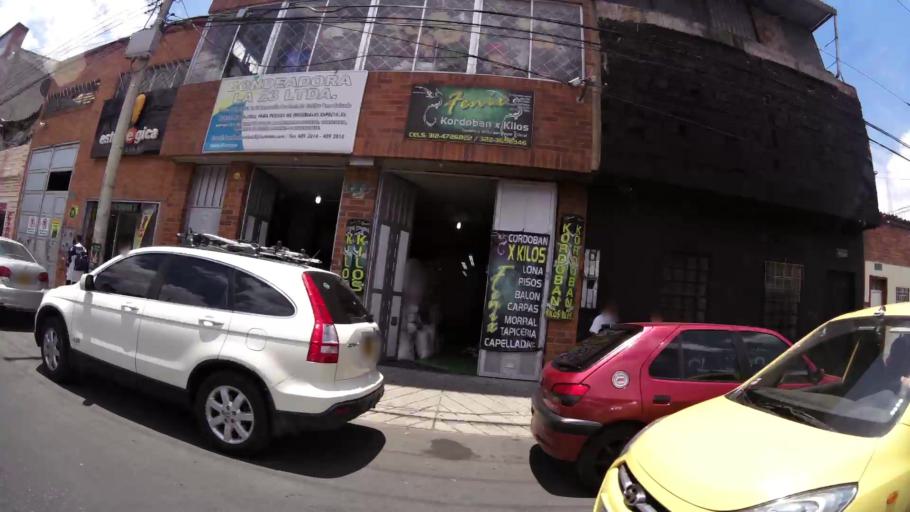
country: CO
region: Bogota D.C.
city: Bogota
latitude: 4.5886
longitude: -74.1026
